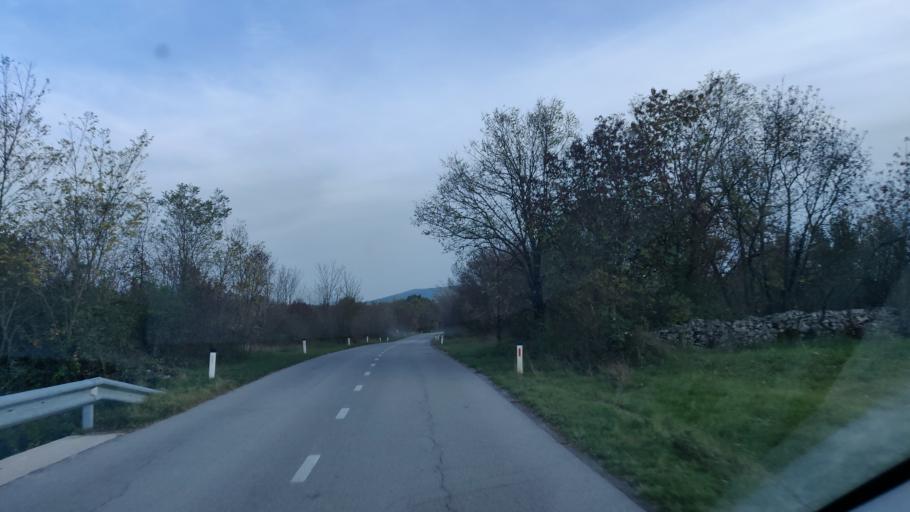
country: SI
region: Sezana
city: Sezana
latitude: 45.7589
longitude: 13.9146
